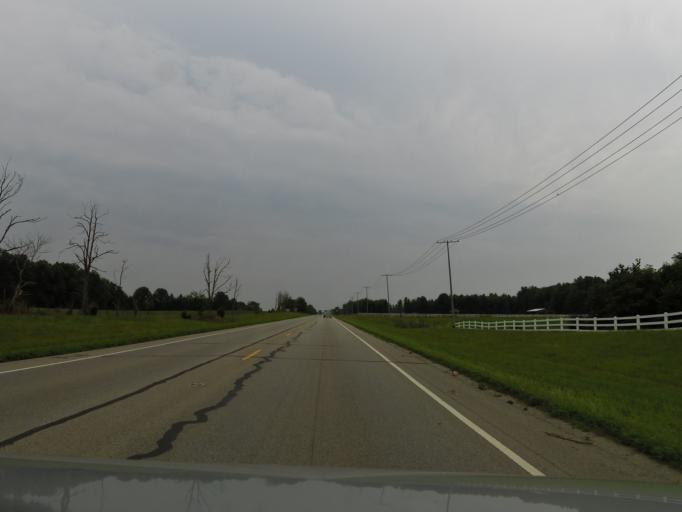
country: US
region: Ohio
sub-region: Brown County
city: Georgetown
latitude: 38.8852
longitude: -83.8921
